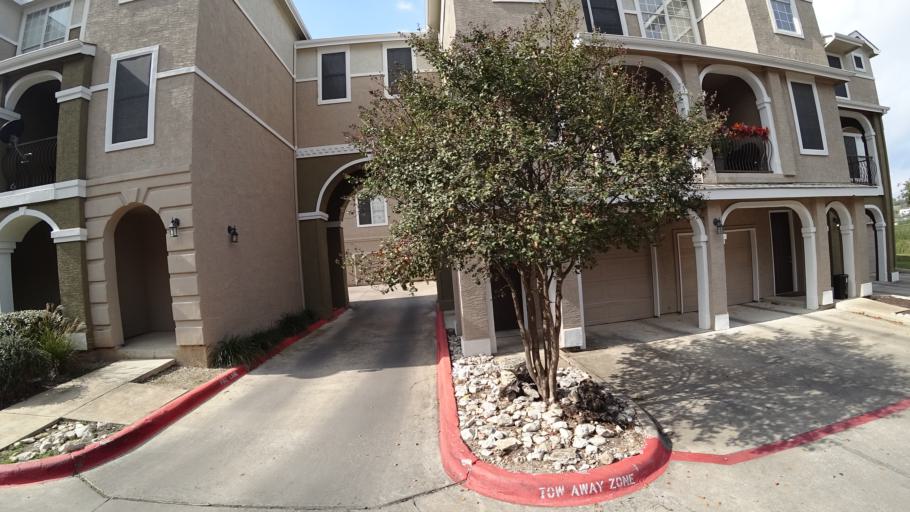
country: US
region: Texas
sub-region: Travis County
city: Hudson Bend
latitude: 30.3851
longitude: -97.8768
